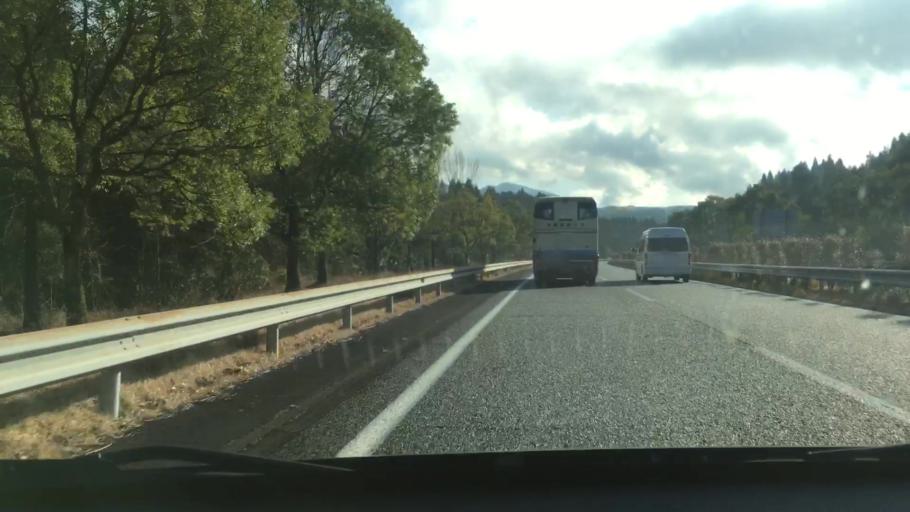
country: JP
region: Kagoshima
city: Okuchi-shinohara
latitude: 32.0328
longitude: 130.7982
